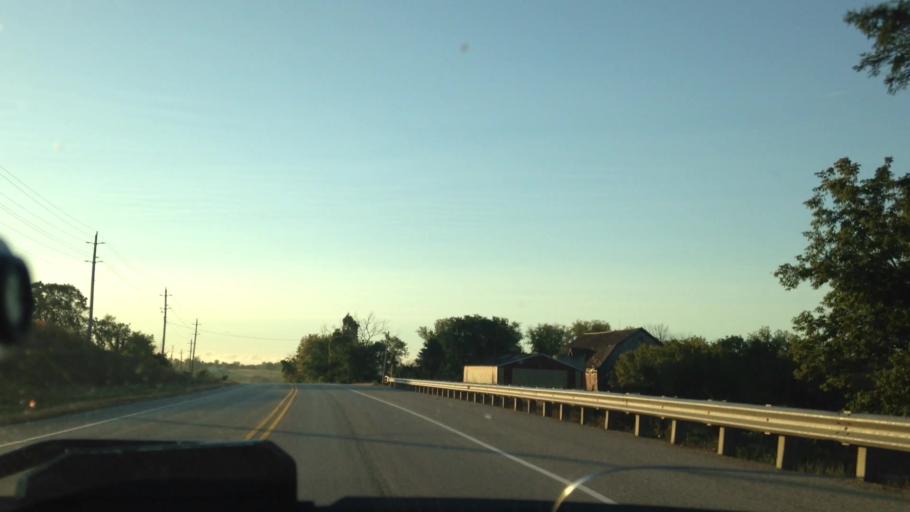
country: US
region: Wisconsin
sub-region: Ozaukee County
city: Saukville
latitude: 43.3918
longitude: -87.9729
